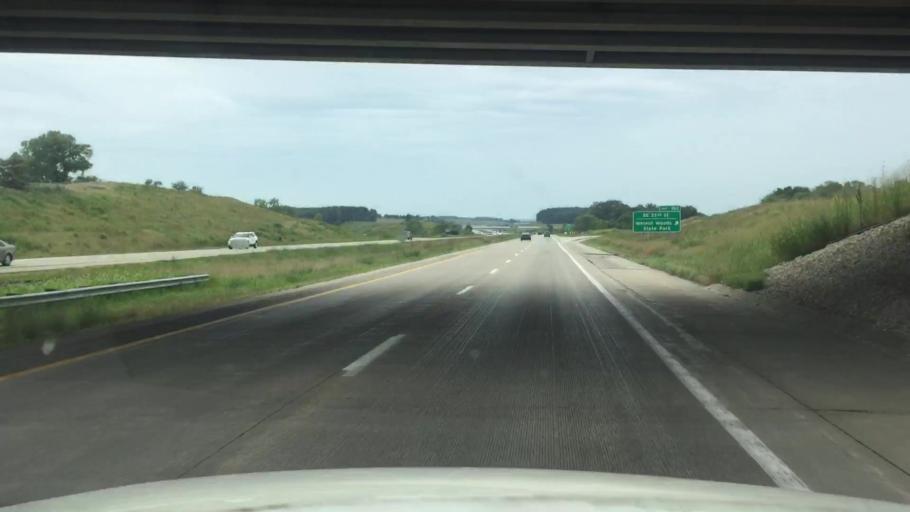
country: US
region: Iowa
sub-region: Polk County
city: West Des Moines
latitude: 41.5226
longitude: -93.7372
